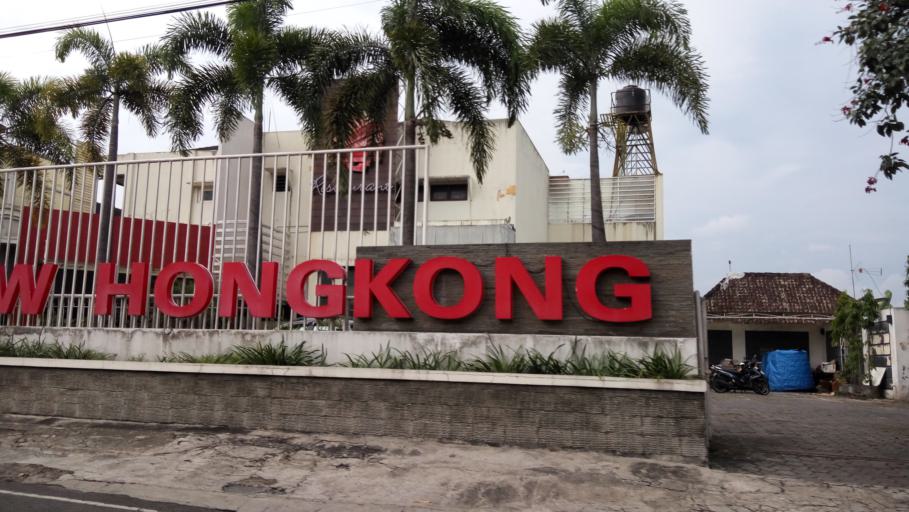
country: ID
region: East Java
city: Malang
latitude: -7.9814
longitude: 112.6292
